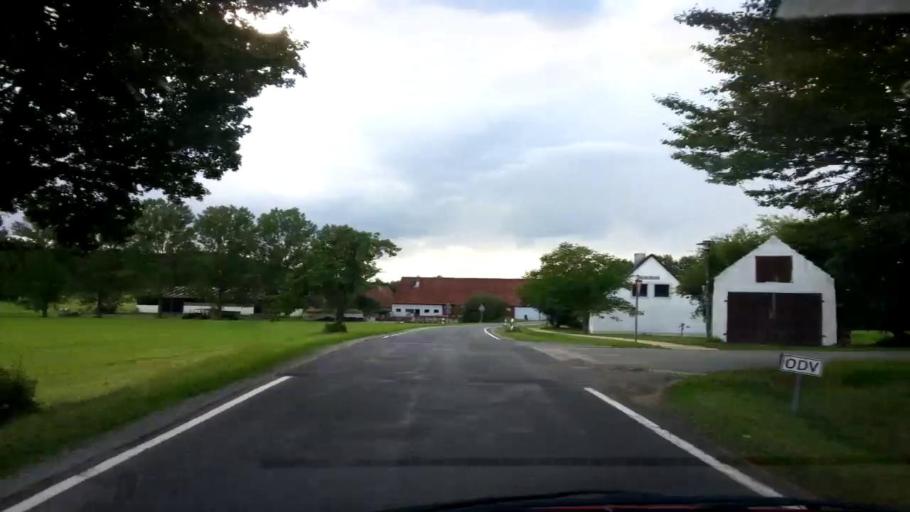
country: DE
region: Bavaria
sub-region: Regierungsbezirk Mittelfranken
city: Burghaslach
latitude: 49.7422
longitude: 10.5657
